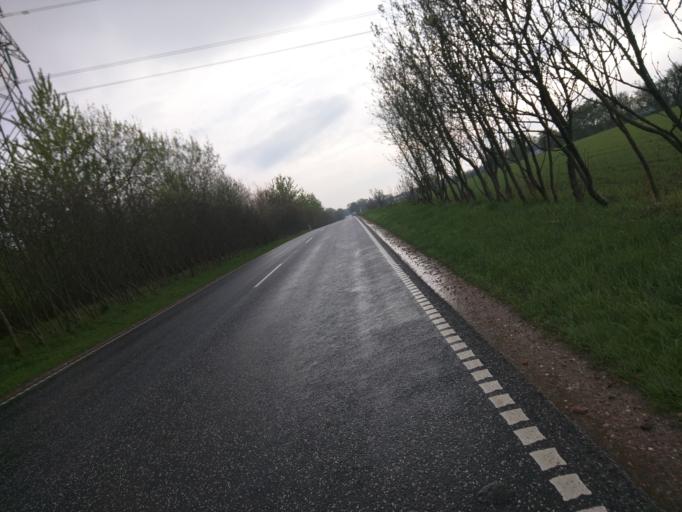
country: DK
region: Central Jutland
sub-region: Viborg Kommune
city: Bjerringbro
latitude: 56.4789
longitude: 9.5611
